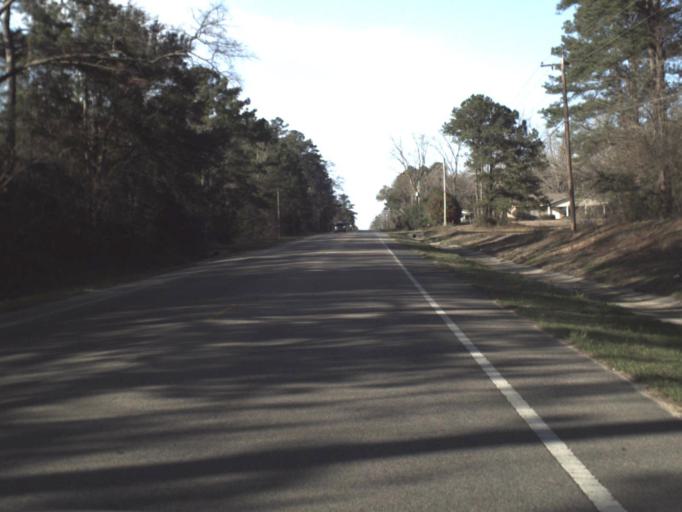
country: US
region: Florida
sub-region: Jackson County
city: Marianna
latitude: 30.7414
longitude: -85.2301
